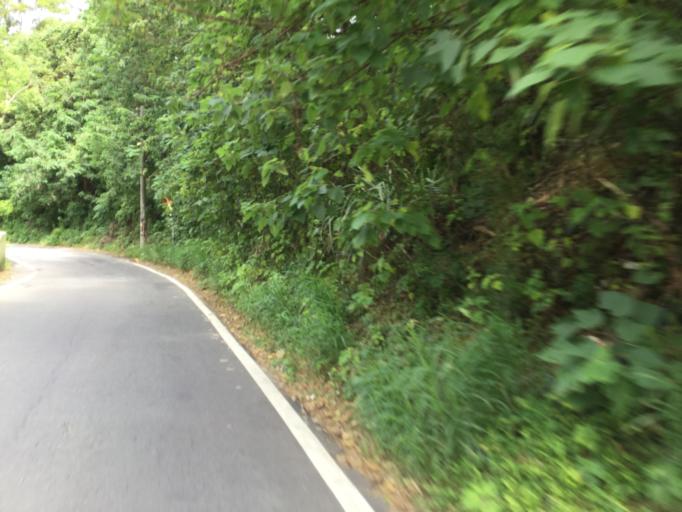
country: TW
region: Taiwan
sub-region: Hsinchu
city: Hsinchu
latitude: 24.7817
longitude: 121.0137
